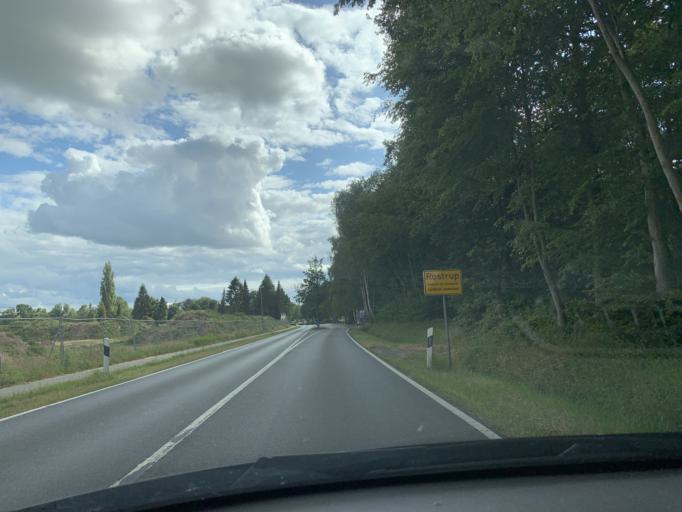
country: DE
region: Lower Saxony
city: Bad Zwischenahn
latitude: 53.2015
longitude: 7.9961
